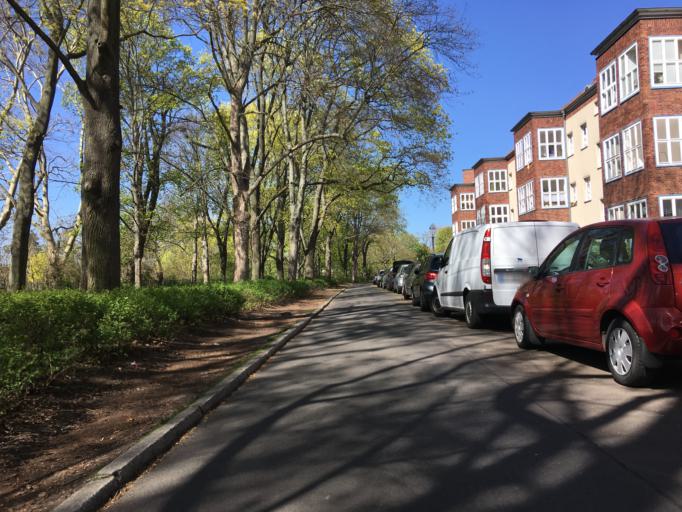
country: DE
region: Berlin
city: Tegel
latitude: 52.5936
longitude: 13.2969
